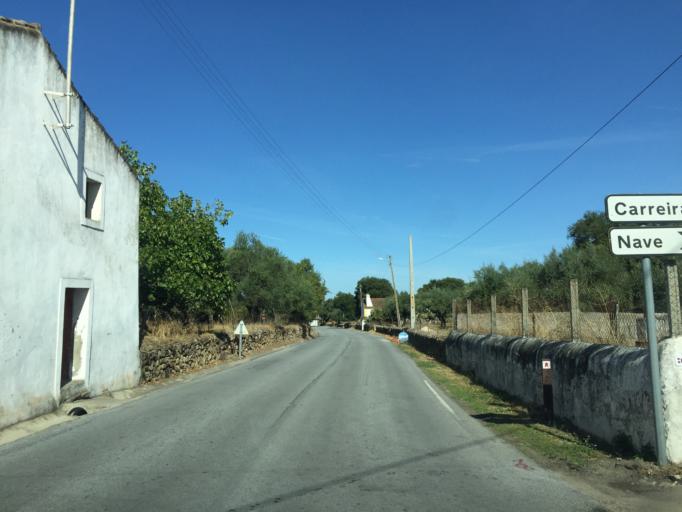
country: PT
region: Portalegre
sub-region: Marvao
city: Marvao
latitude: 39.4246
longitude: -7.3531
